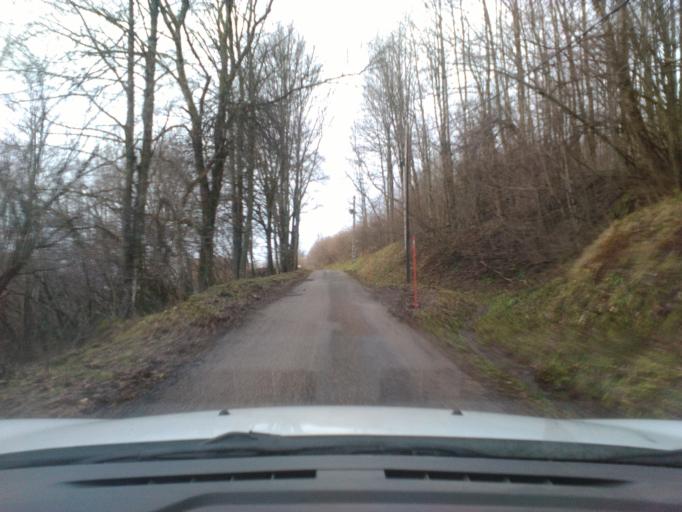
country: FR
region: Lorraine
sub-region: Departement des Vosges
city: Cornimont
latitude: 47.9737
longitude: 6.8523
